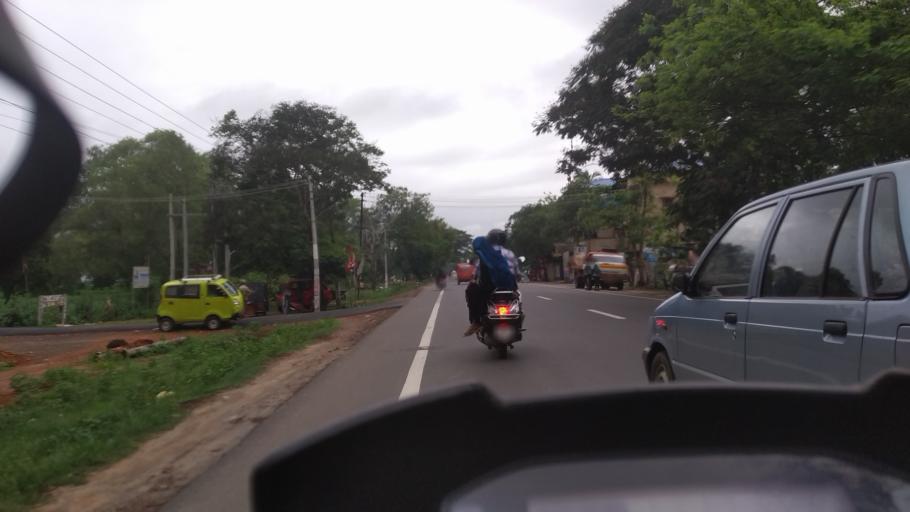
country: IN
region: Kerala
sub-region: Alappuzha
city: Alleppey
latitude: 9.4463
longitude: 76.3426
